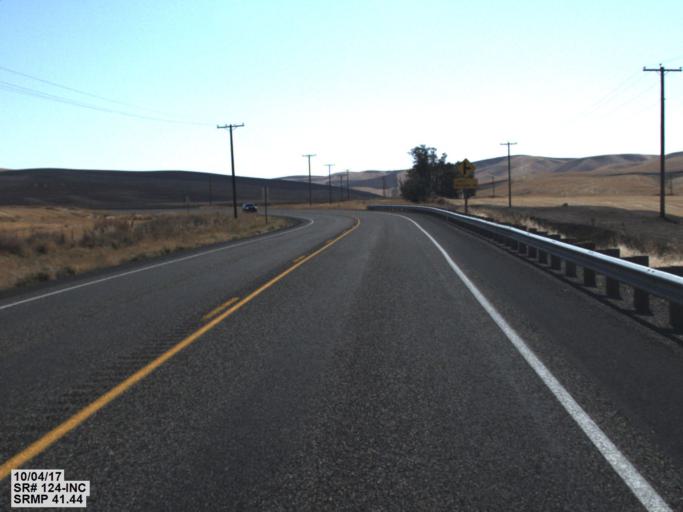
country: US
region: Washington
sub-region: Walla Walla County
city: Waitsburg
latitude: 46.2704
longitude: -118.2211
